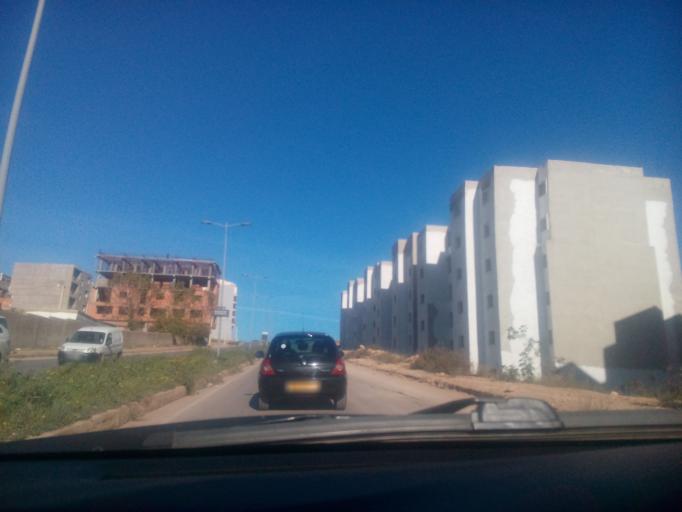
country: DZ
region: Oran
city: Bir el Djir
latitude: 35.7443
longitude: -0.5486
